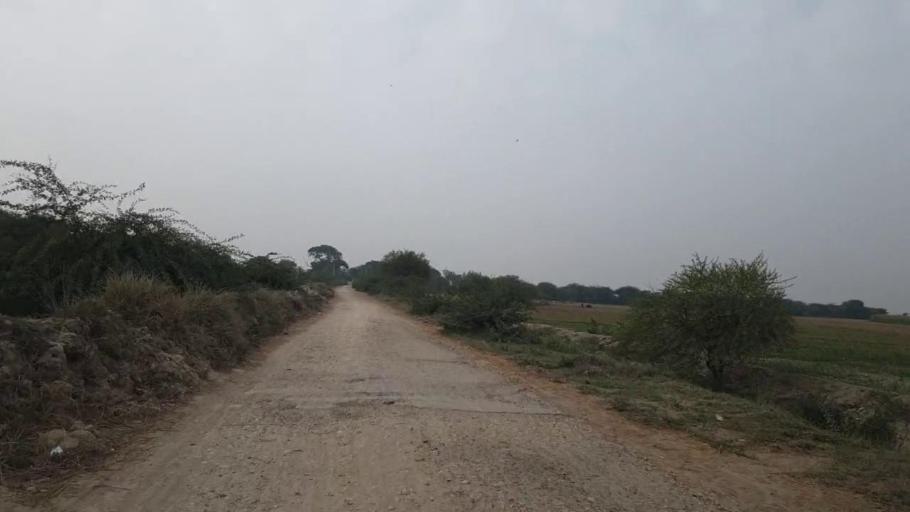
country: PK
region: Sindh
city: Kario
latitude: 24.9110
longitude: 68.5381
